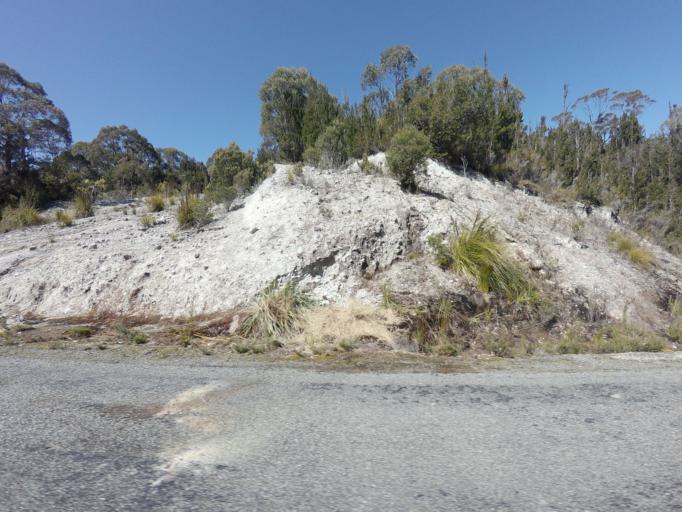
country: AU
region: Tasmania
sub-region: Derwent Valley
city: New Norfolk
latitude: -42.7626
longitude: 146.3965
